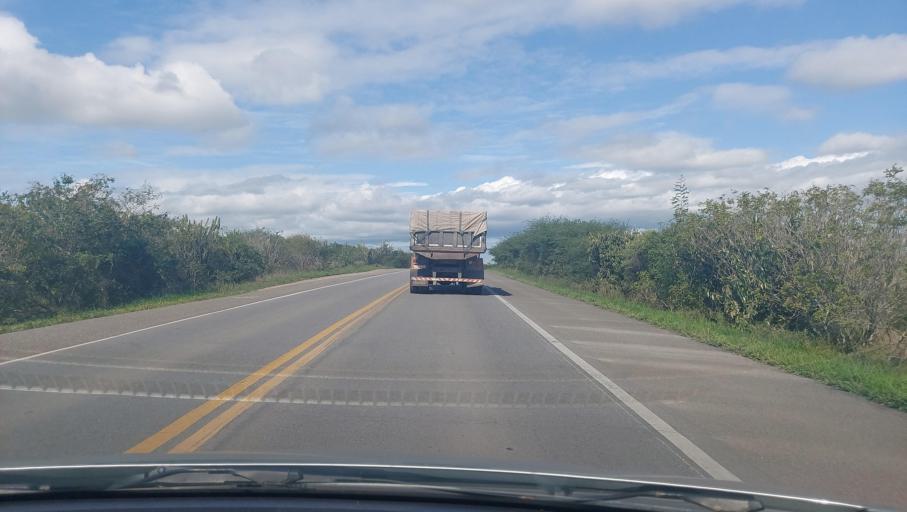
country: BR
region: Bahia
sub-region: Ipira
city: Ipira
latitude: -12.4885
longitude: -39.6913
